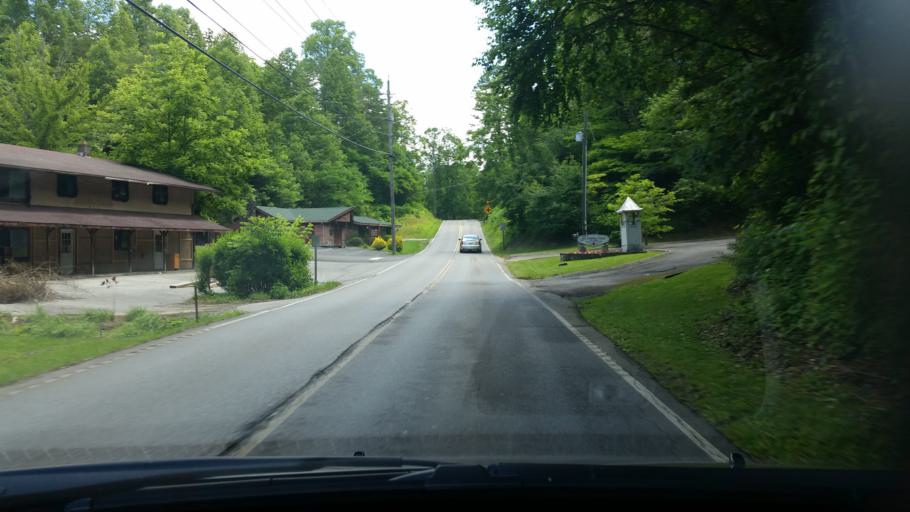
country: US
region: Tennessee
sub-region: Sevier County
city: Gatlinburg
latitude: 35.7395
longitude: -83.4643
